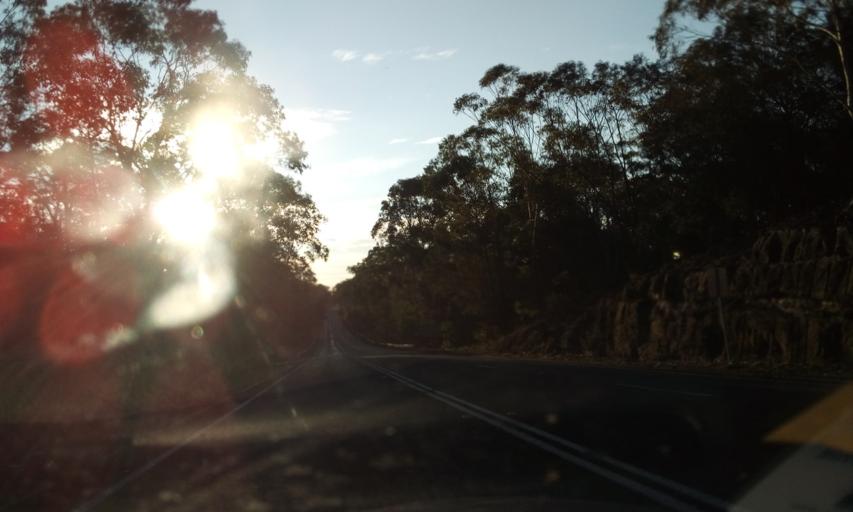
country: AU
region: New South Wales
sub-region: Wollondilly
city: Douglas Park
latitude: -34.2410
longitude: 150.7085
